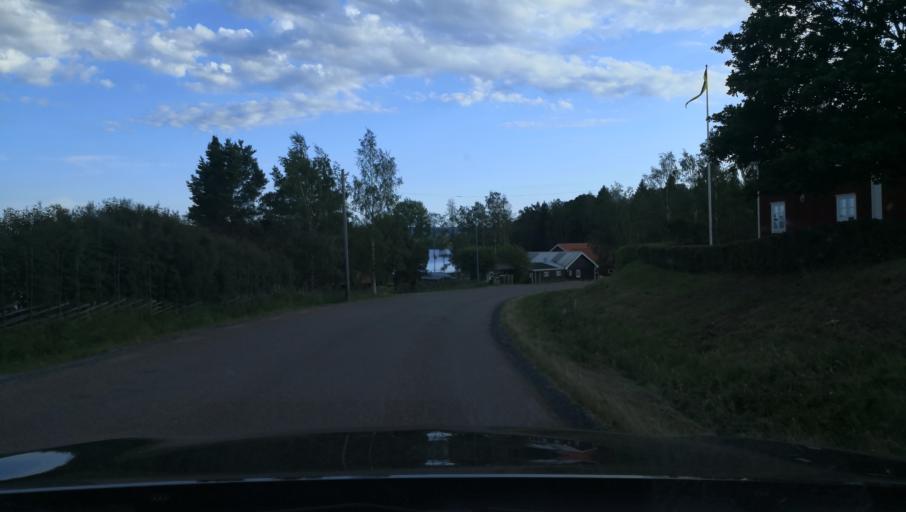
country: SE
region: Dalarna
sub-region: Ludvika Kommun
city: Ludvika
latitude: 60.1009
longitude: 15.2337
